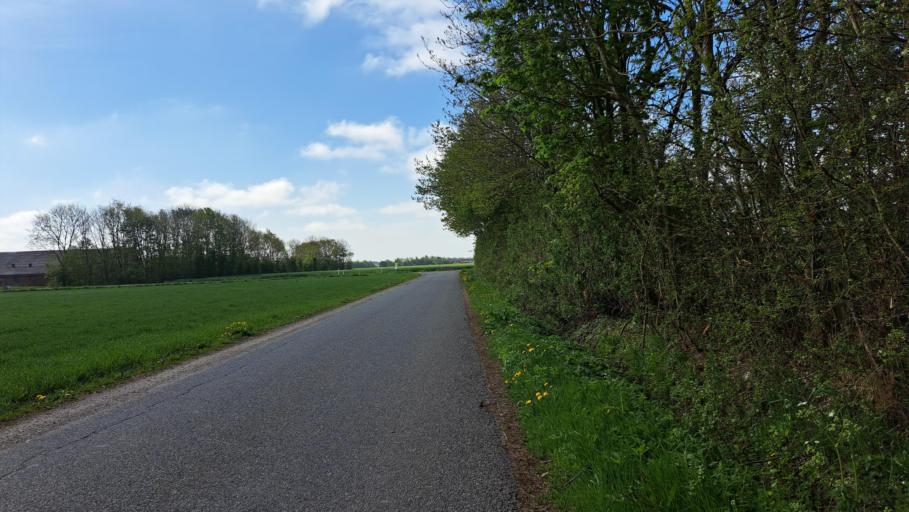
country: DK
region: Central Jutland
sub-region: Hedensted Kommune
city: Hedensted
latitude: 55.8015
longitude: 9.6561
